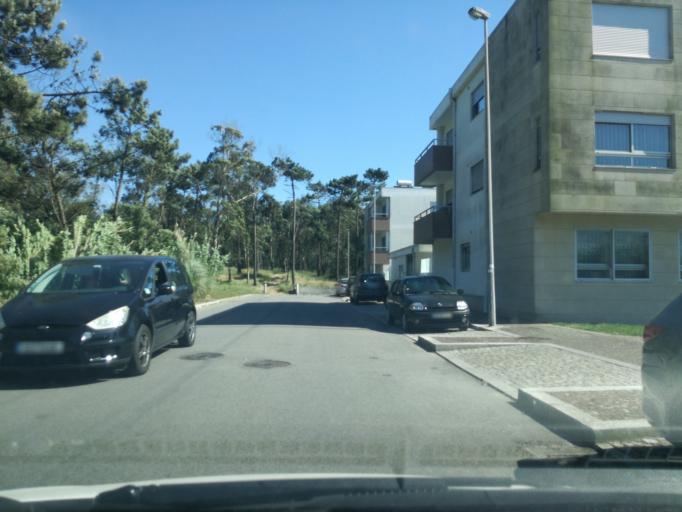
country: PT
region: Porto
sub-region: Matosinhos
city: Lavra
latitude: 41.2742
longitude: -8.7228
